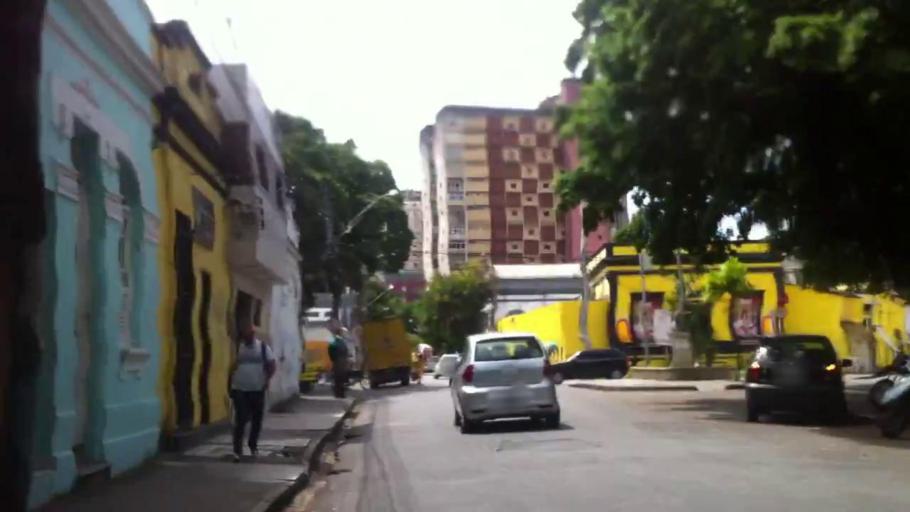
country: BR
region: Pernambuco
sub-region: Recife
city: Recife
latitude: -8.0580
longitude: -34.8863
